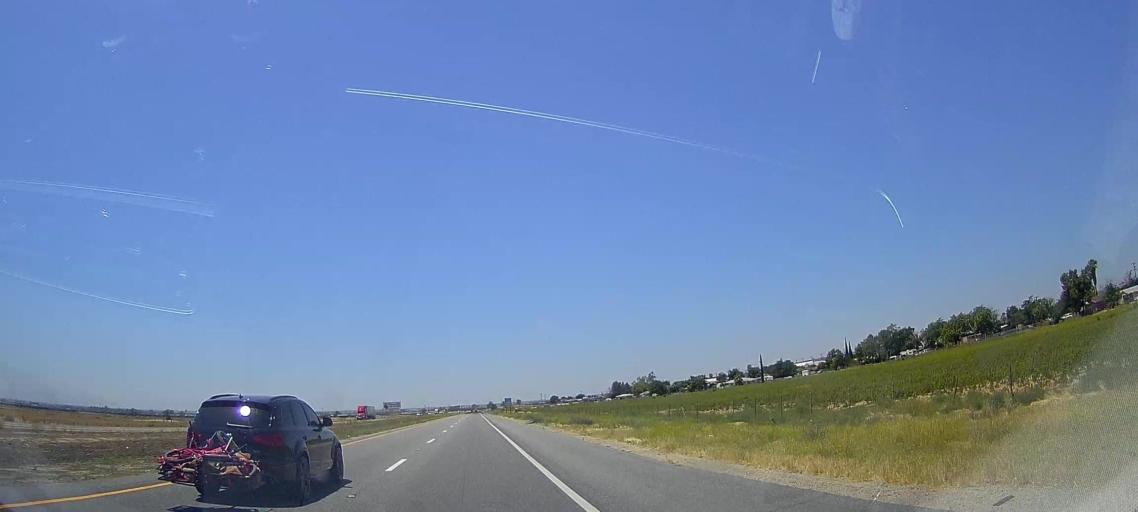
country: US
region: California
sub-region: Kern County
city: Lamont
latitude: 35.3439
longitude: -118.8672
